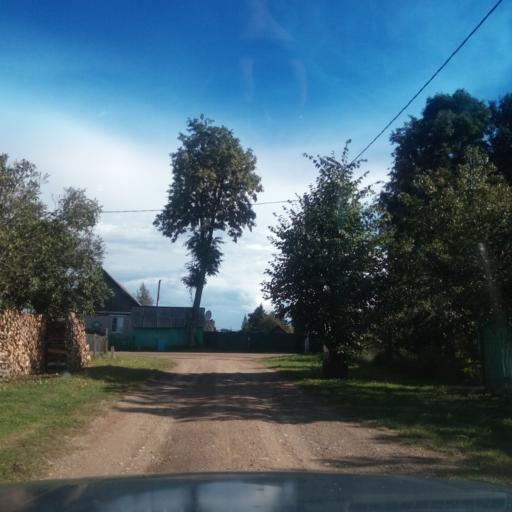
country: BY
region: Vitebsk
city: Dzisna
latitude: 55.6743
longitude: 28.3271
